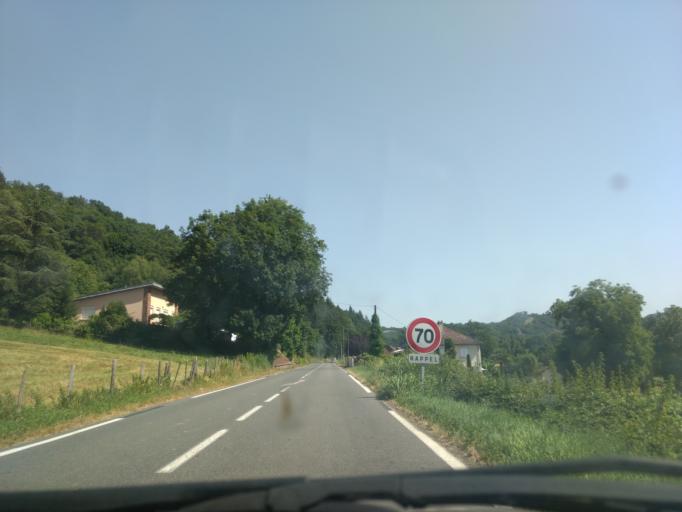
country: FR
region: Midi-Pyrenees
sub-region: Departement de l'Aveyron
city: Livinhac-le-Haut
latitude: 44.6026
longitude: 2.2452
